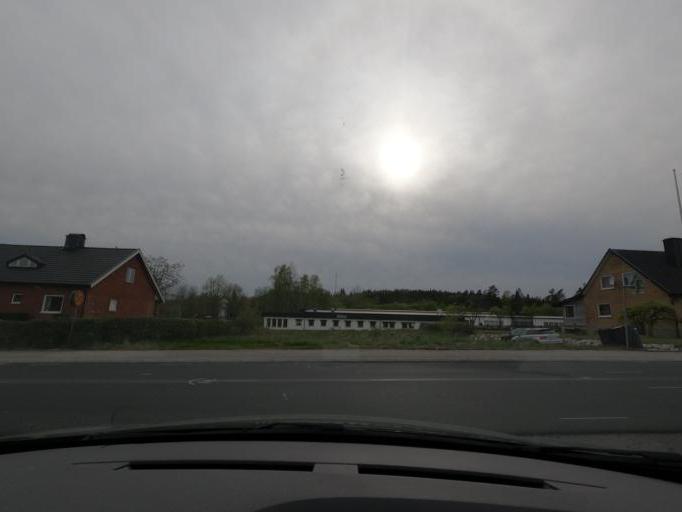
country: SE
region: Joenkoeping
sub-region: Varnamo Kommun
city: Bredaryd
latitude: 57.2232
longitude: 13.7836
